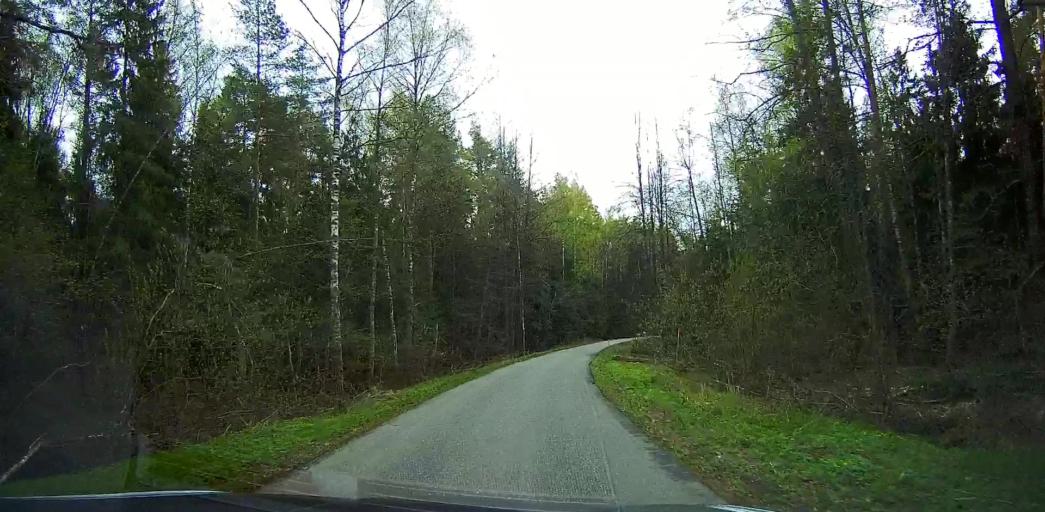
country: RU
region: Moskovskaya
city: Malyshevo
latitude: 55.5421
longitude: 38.3861
